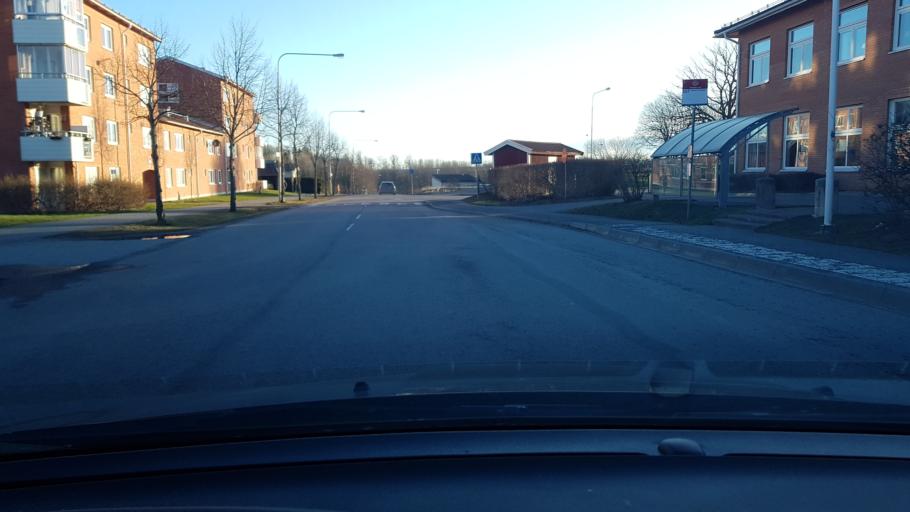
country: SE
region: Stockholm
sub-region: Norrtalje Kommun
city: Norrtalje
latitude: 59.7472
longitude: 18.6923
